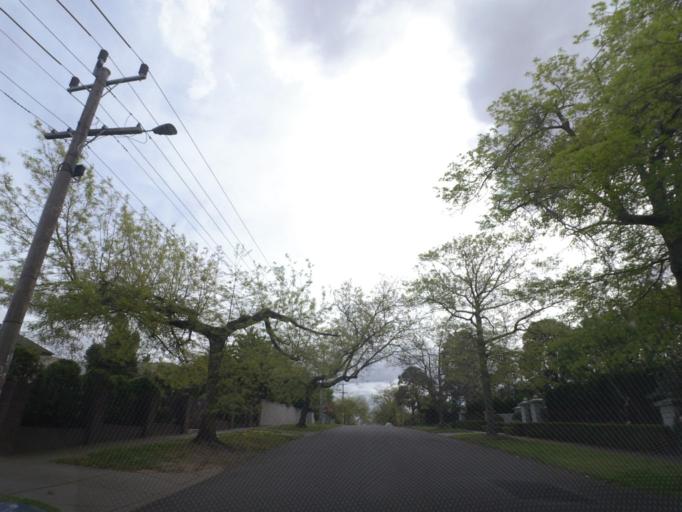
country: AU
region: Victoria
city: Mont Albert
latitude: -37.8103
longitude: 145.0981
